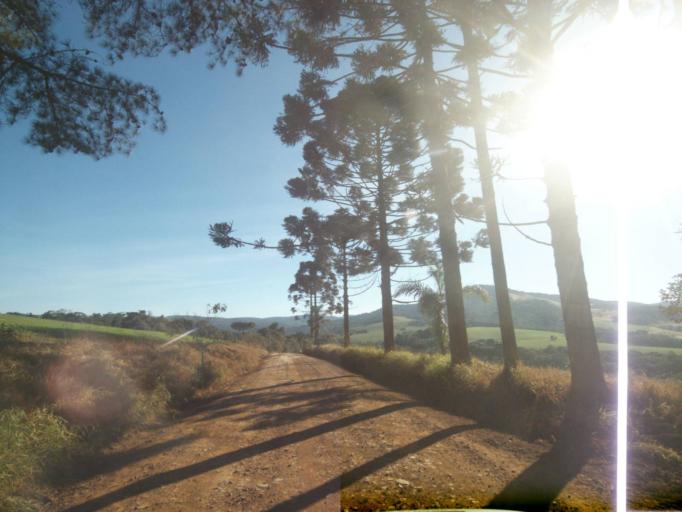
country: BR
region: Parana
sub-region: Tibagi
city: Tibagi
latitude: -24.5229
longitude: -50.5000
